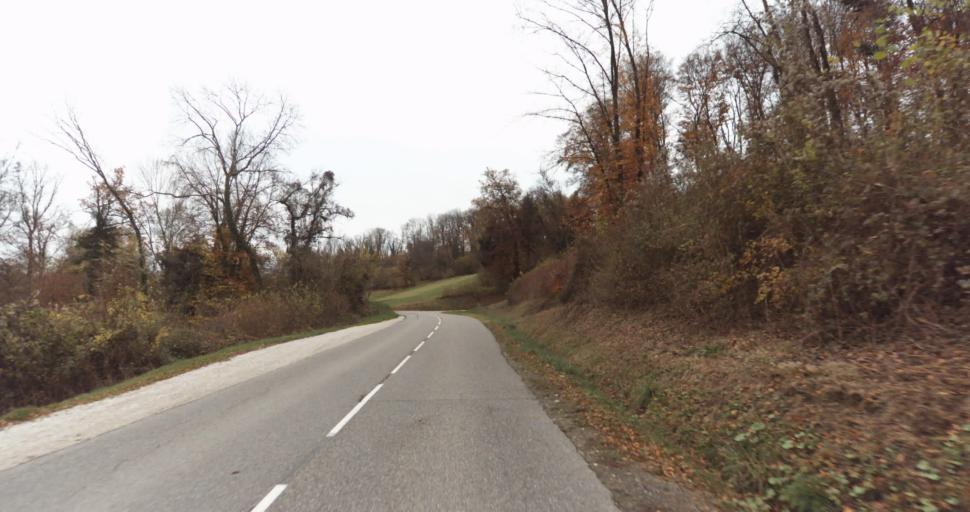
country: FR
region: Rhone-Alpes
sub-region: Departement de la Haute-Savoie
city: Chavanod
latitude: 45.8949
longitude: 6.0411
